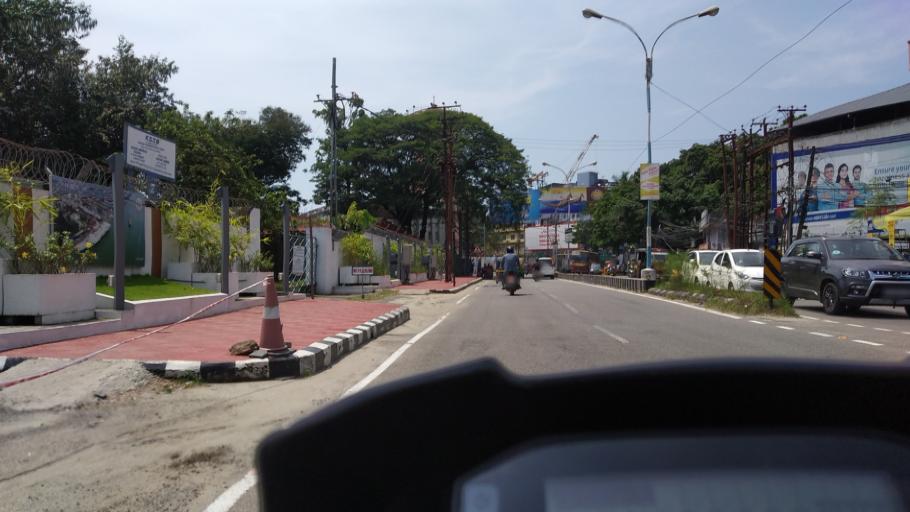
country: IN
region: Kerala
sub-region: Ernakulam
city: Cochin
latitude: 9.9568
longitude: 76.2908
